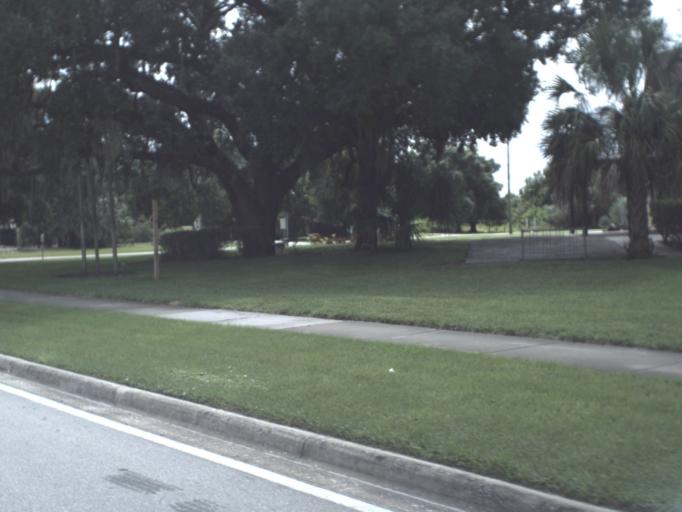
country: US
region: Florida
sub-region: DeSoto County
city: Arcadia
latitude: 27.2106
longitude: -81.8466
